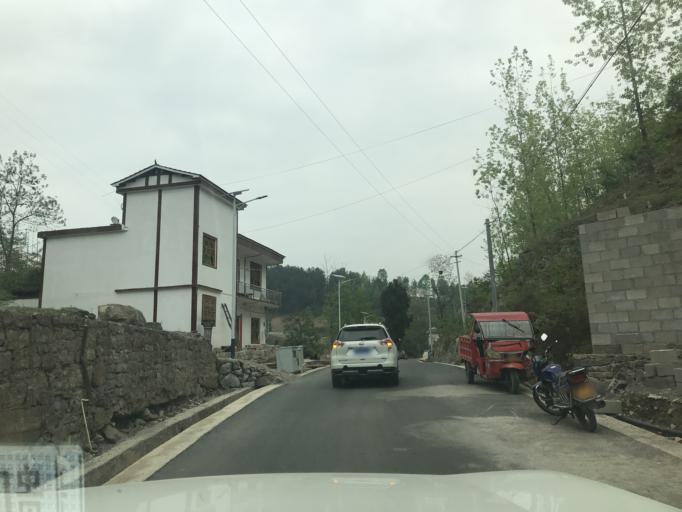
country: CN
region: Guizhou Sheng
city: Tongjing
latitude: 28.3055
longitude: 108.2684
